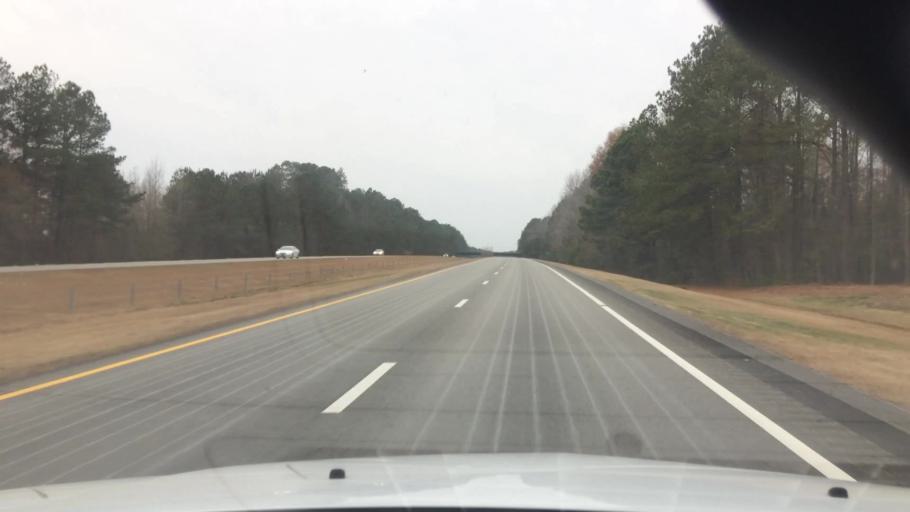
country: US
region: North Carolina
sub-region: Nash County
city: Spring Hope
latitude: 35.9325
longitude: -78.1113
